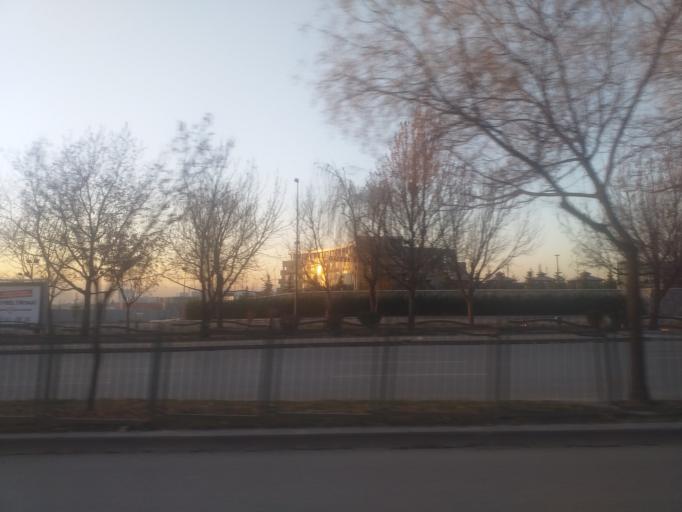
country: TR
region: Ankara
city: Ankara
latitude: 39.9690
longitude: 32.8211
